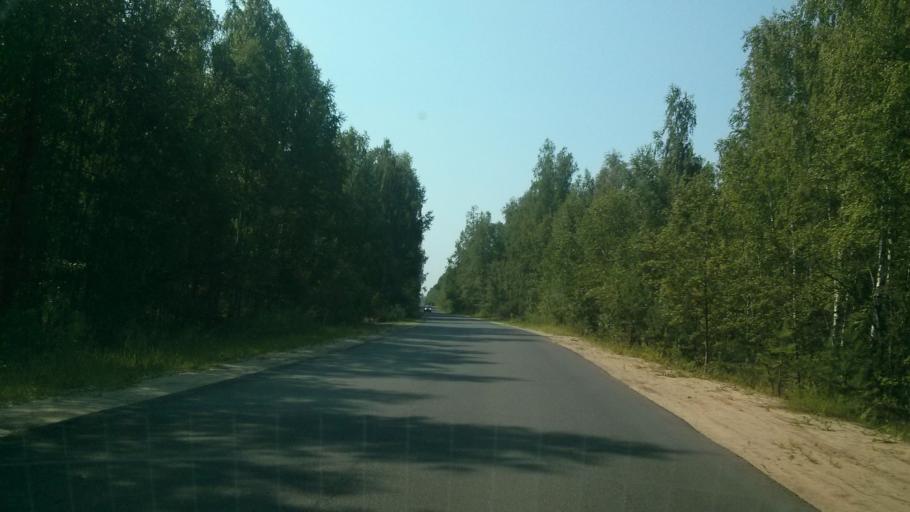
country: RU
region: Vladimir
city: Murom
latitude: 55.5198
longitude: 42.0205
